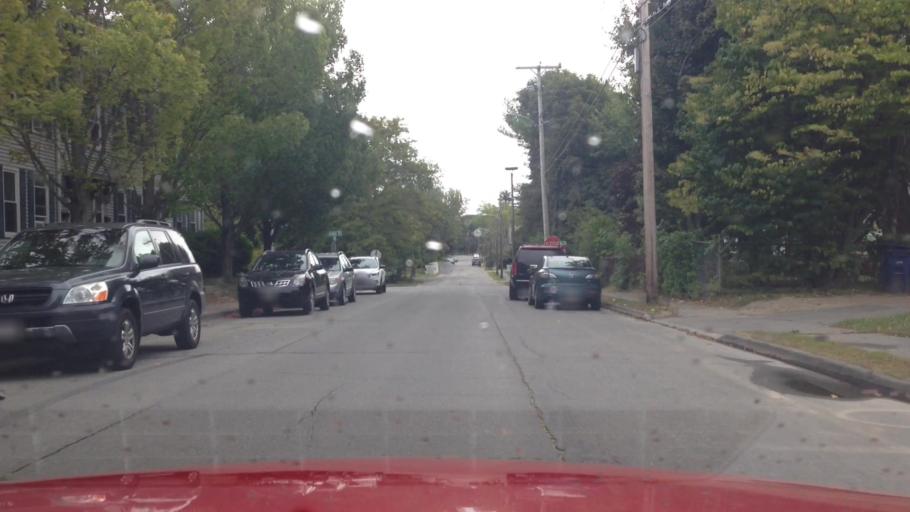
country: US
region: Maine
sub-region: Cumberland County
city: Westbrook
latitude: 43.6772
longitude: -70.3498
